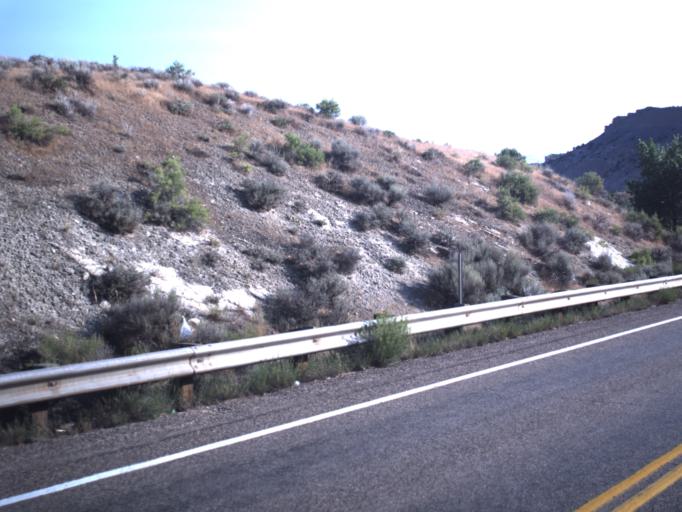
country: US
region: Utah
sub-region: Uintah County
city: Vernal
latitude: 40.5170
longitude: -109.5239
